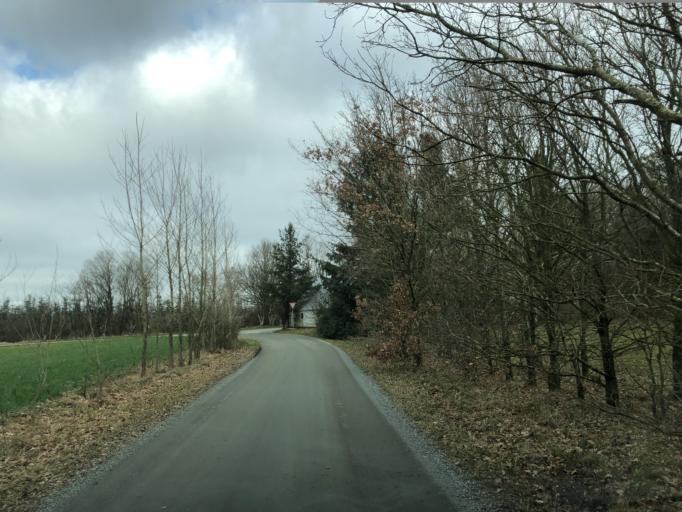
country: DK
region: South Denmark
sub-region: Billund Kommune
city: Billund
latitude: 55.7817
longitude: 9.1348
